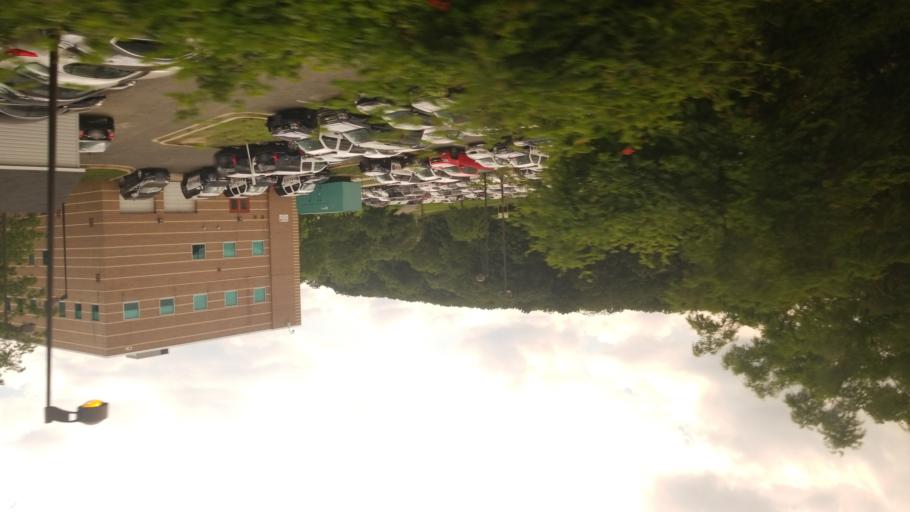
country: US
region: Maryland
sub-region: Prince George's County
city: Chillum
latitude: 38.9544
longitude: -77.0034
